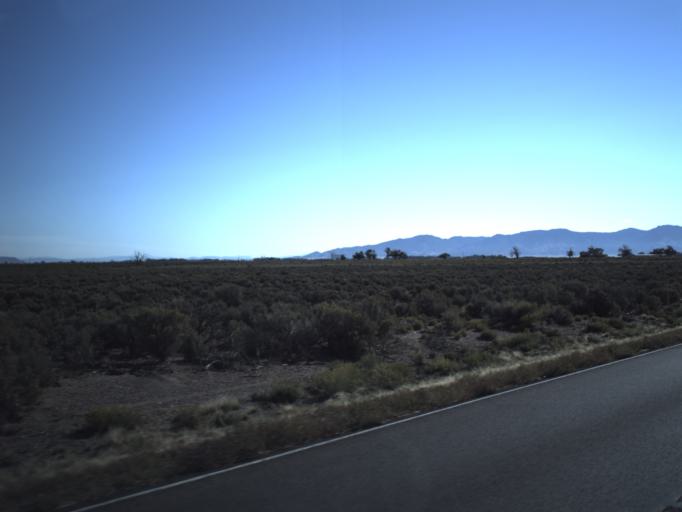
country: US
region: Utah
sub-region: Washington County
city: Enterprise
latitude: 37.7272
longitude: -113.7057
